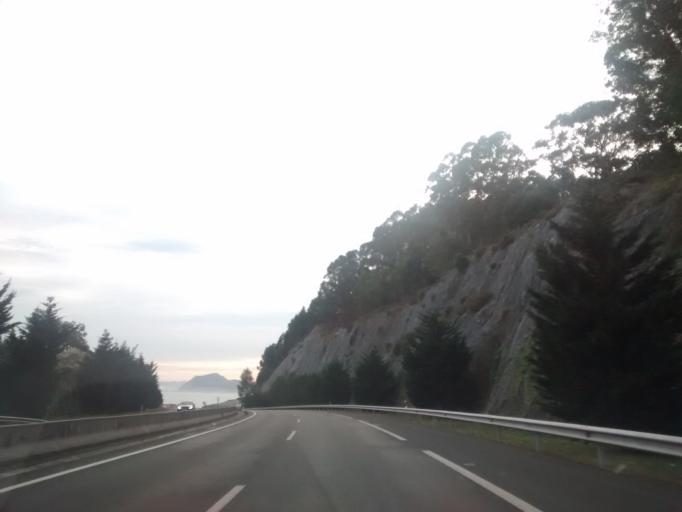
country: ES
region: Cantabria
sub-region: Provincia de Cantabria
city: Castro-Urdiales
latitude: 43.3781
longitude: -3.2276
